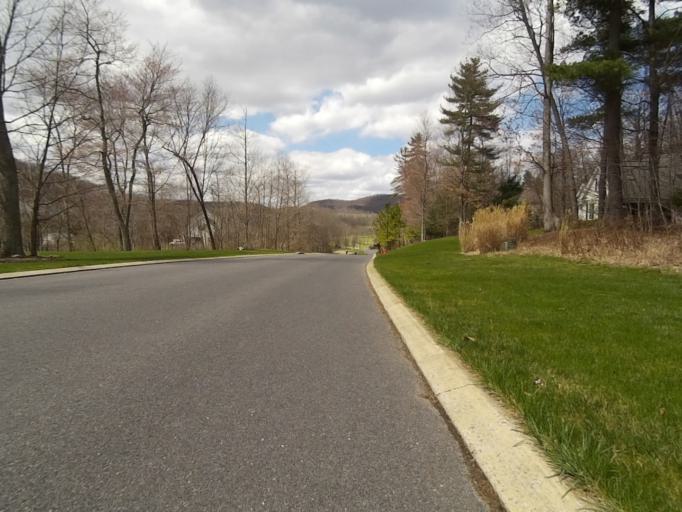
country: US
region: Pennsylvania
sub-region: Centre County
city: Park Forest Village
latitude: 40.8269
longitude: -77.9320
